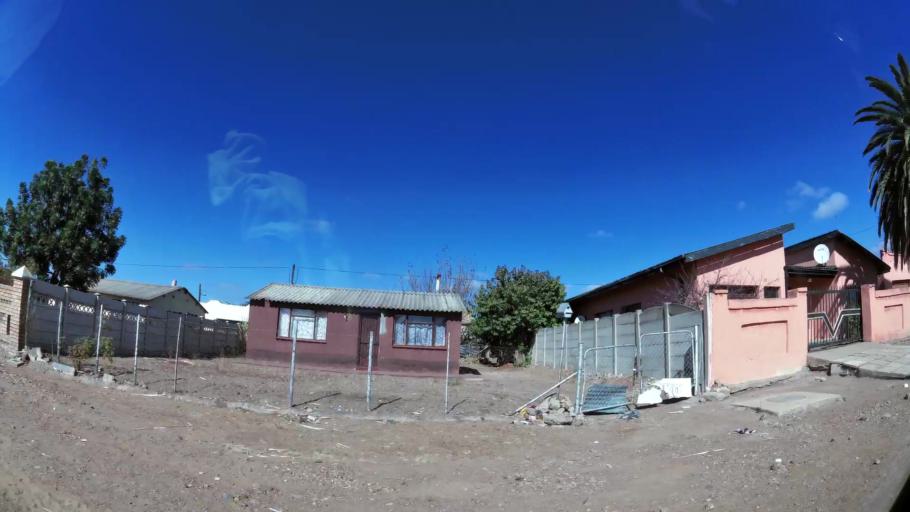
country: ZA
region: Limpopo
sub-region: Capricorn District Municipality
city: Polokwane
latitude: -23.8659
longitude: 29.3927
